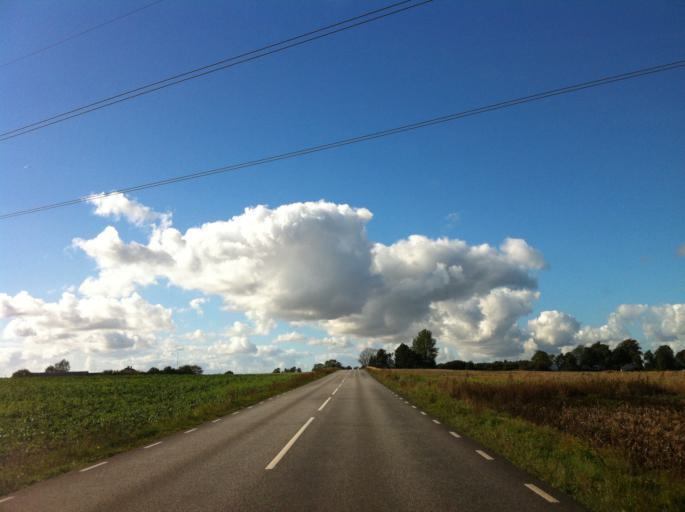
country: SE
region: Skane
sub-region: Hoors Kommun
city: Loberod
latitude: 55.7434
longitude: 13.4179
